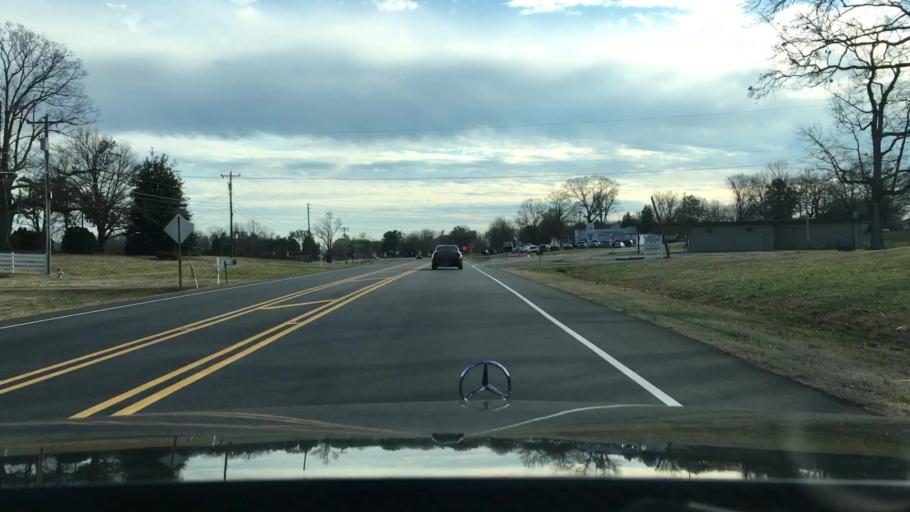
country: US
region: Virginia
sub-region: City of Danville
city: Danville
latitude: 36.5355
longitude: -79.4001
